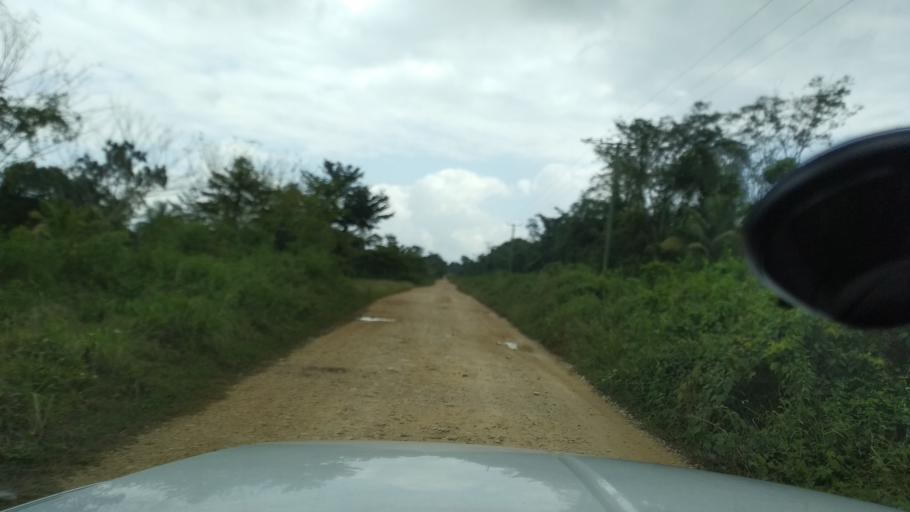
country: BZ
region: Toledo
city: Punta Gorda
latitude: 16.2180
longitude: -89.0020
